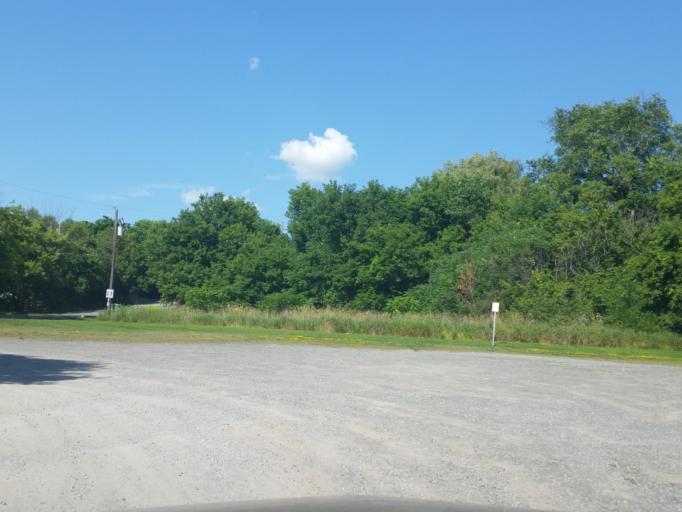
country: CA
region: Ontario
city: Ottawa
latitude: 45.3153
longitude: -75.6956
